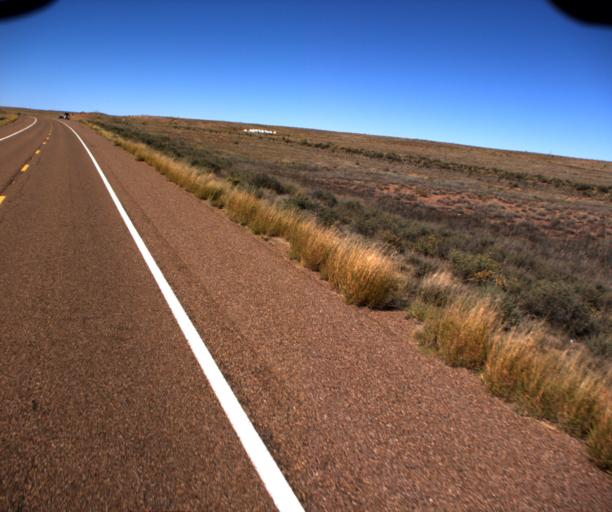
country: US
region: Arizona
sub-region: Navajo County
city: Holbrook
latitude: 34.8444
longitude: -109.9514
